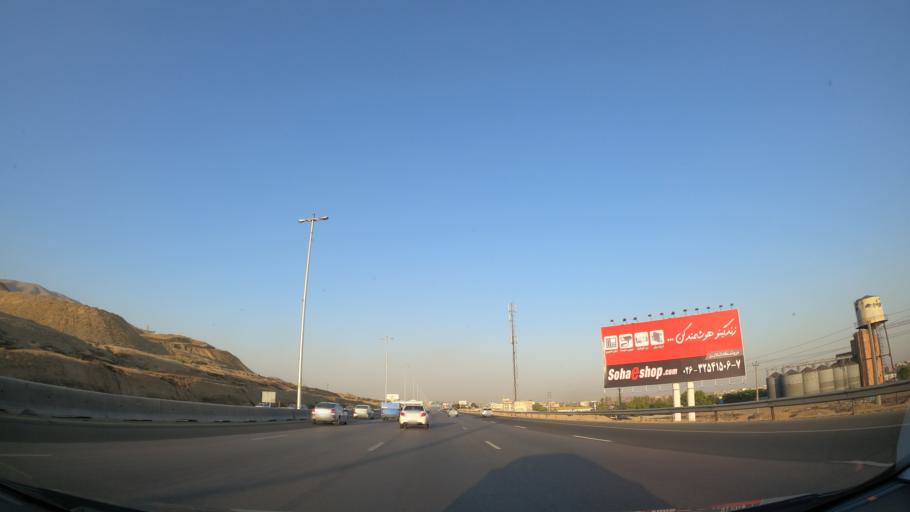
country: IR
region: Tehran
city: Shahr-e Qods
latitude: 35.7438
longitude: 51.0983
